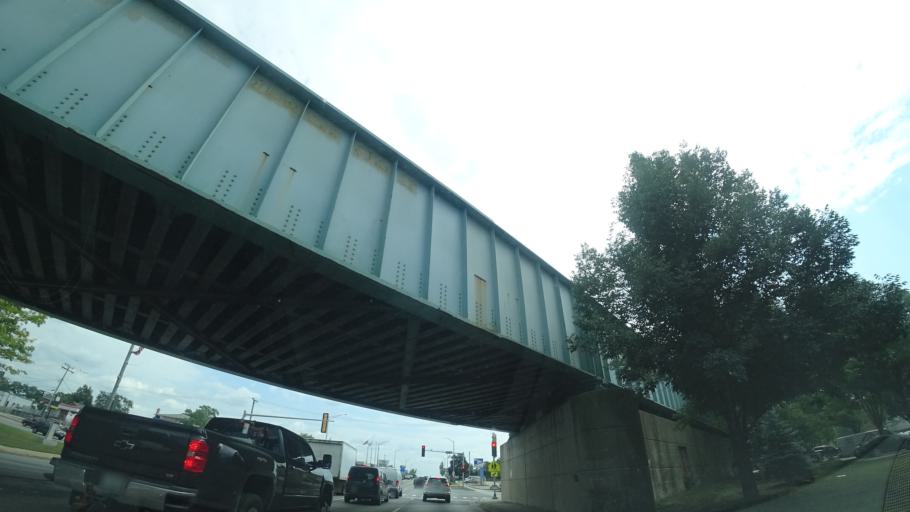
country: US
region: Illinois
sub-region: Cook County
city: Worth
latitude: 41.6904
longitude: -87.7975
